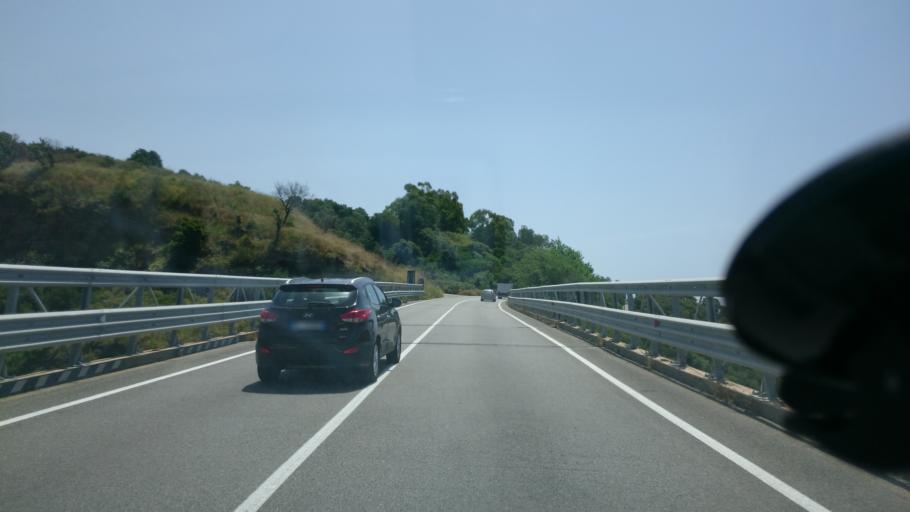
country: IT
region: Calabria
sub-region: Provincia di Cosenza
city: Cittadella del Capo
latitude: 39.5426
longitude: 15.8921
